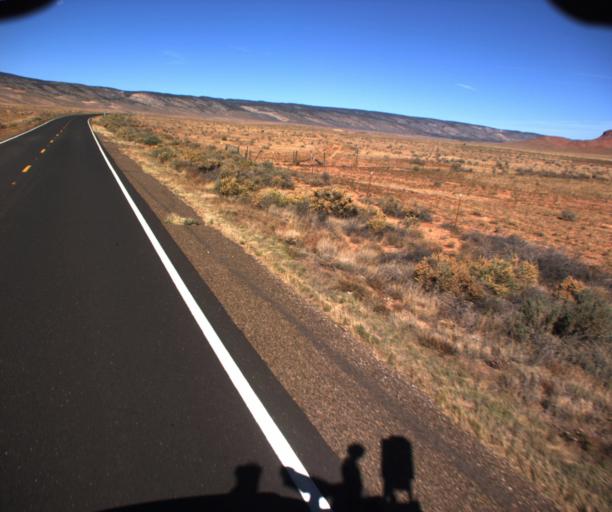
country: US
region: Arizona
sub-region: Coconino County
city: Fredonia
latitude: 36.7172
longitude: -112.0001
